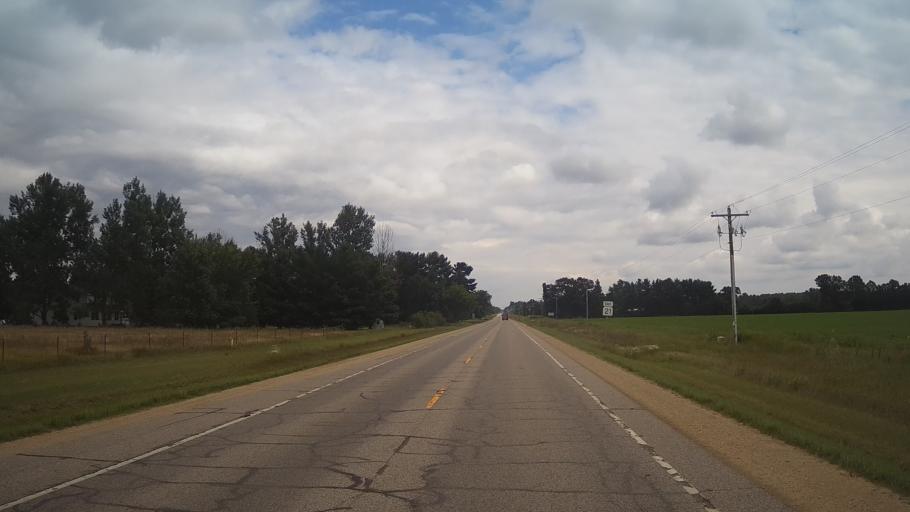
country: US
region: Wisconsin
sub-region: Waushara County
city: Wautoma
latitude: 44.0684
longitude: -89.3523
